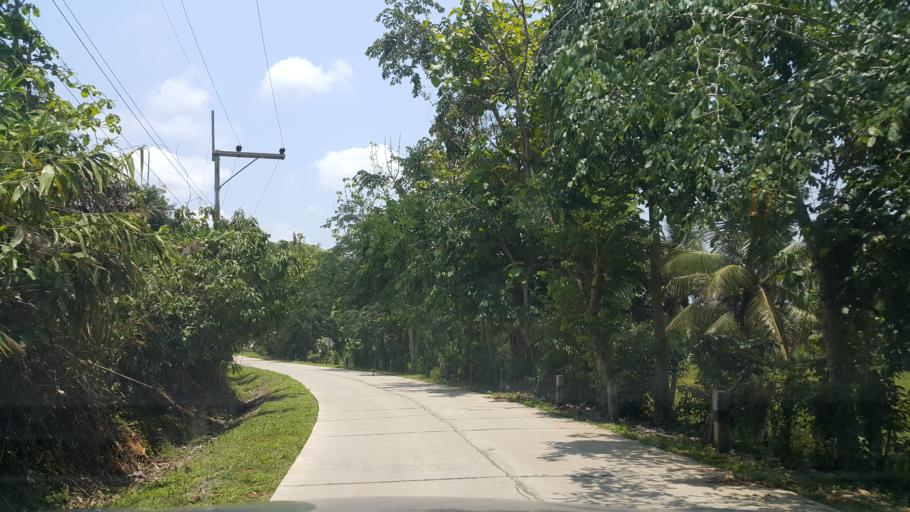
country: TH
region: Chiang Rai
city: Chiang Rai
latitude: 19.9761
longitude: 99.7490
